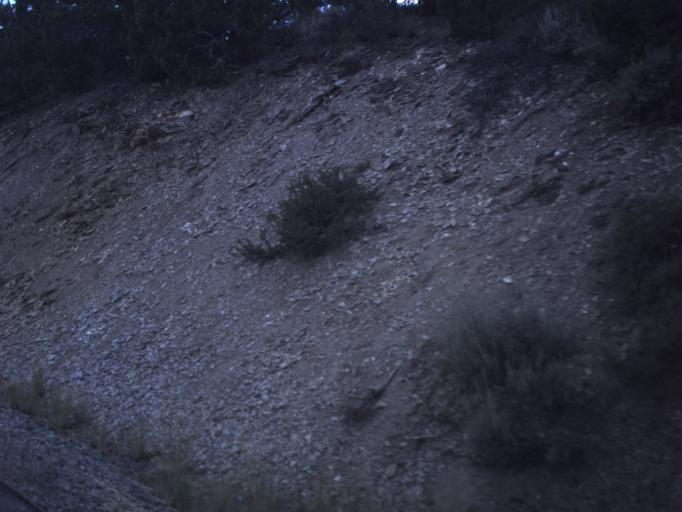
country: US
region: Utah
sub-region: Tooele County
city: Grantsville
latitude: 40.3423
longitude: -112.5670
